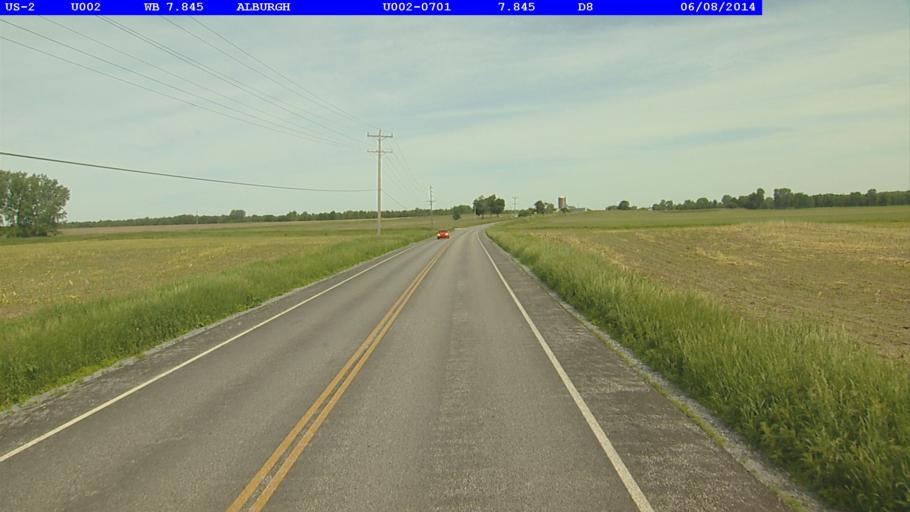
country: US
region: New York
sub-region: Clinton County
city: Rouses Point
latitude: 44.9379
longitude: -73.2740
